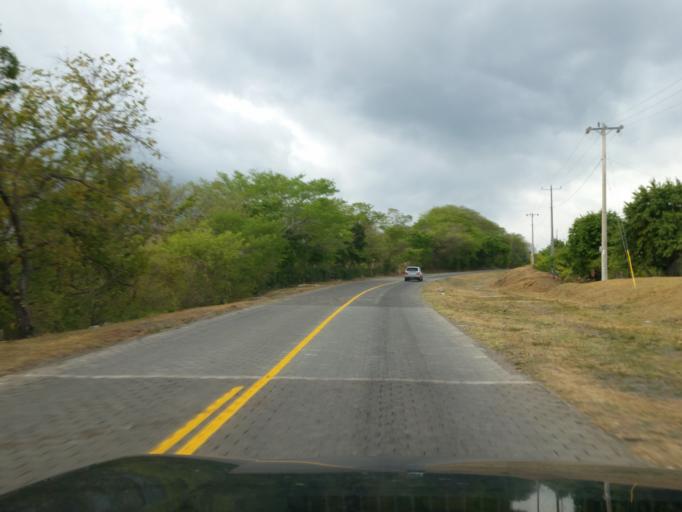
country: NI
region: Managua
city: San Rafael del Sur
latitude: 11.8766
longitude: -86.5154
